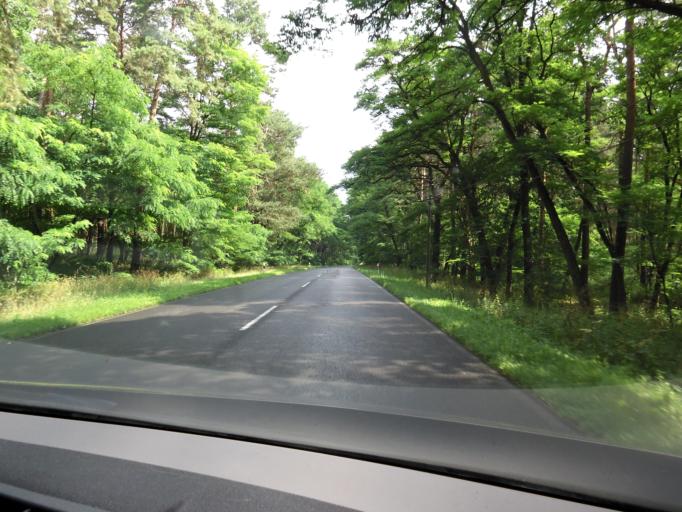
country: DE
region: Saxony-Anhalt
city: Kemberg
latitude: 51.7401
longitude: 12.6235
